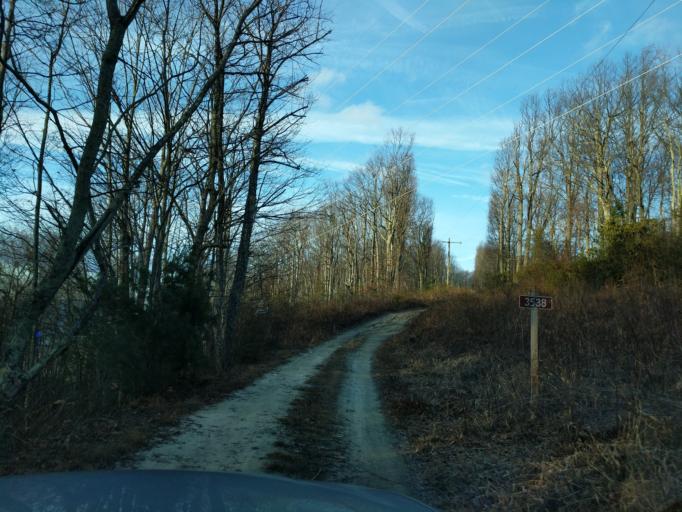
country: US
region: North Carolina
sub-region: Haywood County
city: Cove Creek
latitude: 35.7292
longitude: -83.0537
